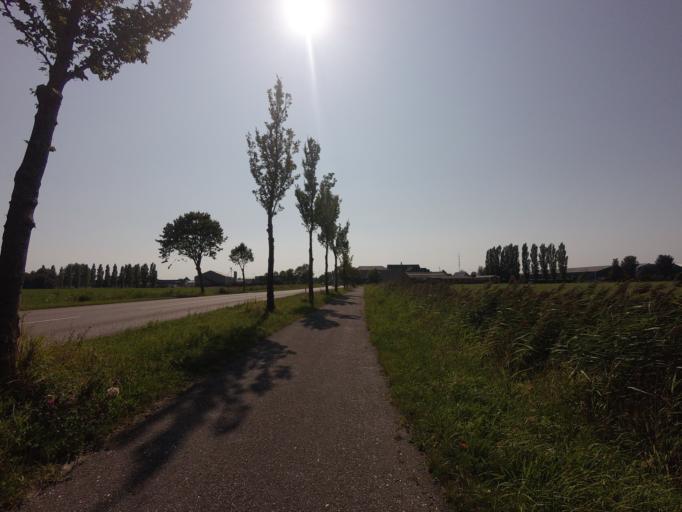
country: NL
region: Groningen
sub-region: Gemeente Zuidhorn
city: Grijpskerk
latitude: 53.2694
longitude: 6.3076
